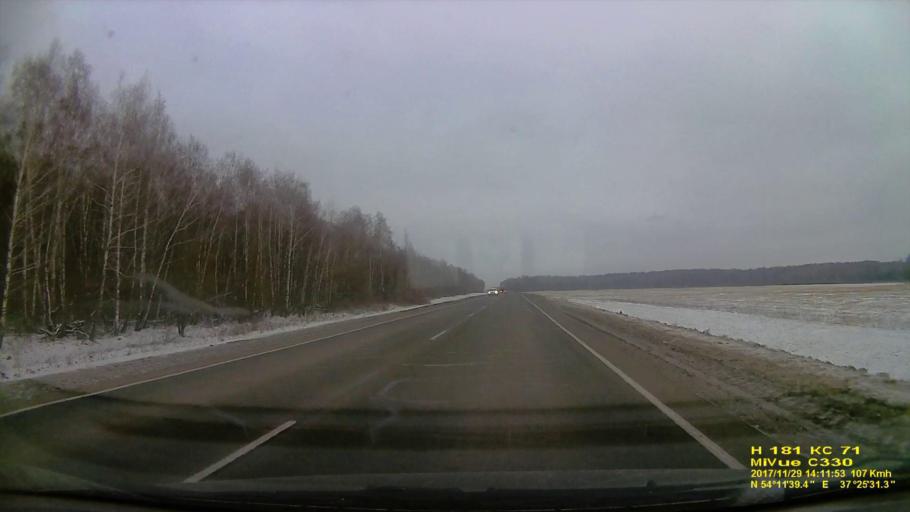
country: RU
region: Tula
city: Barsuki
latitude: 54.1940
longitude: 37.4257
